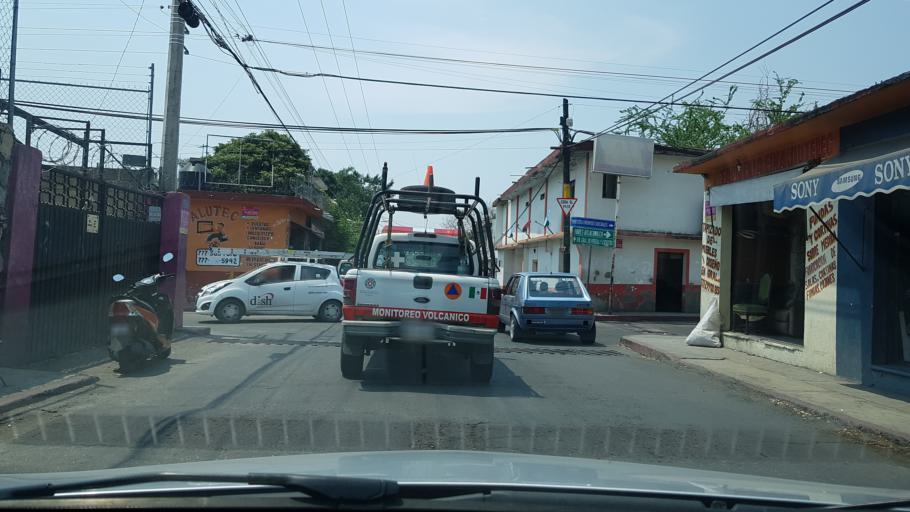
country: MX
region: Morelos
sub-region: Jiutepec
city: Jiutepec
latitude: 18.8858
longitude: -99.1769
